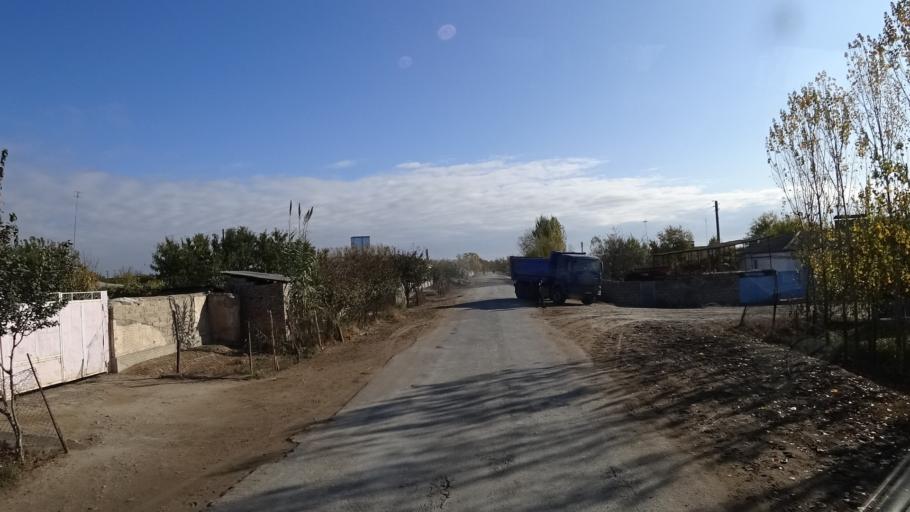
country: UZ
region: Sirdaryo
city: Sirdaryo
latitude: 40.9035
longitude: 68.6849
